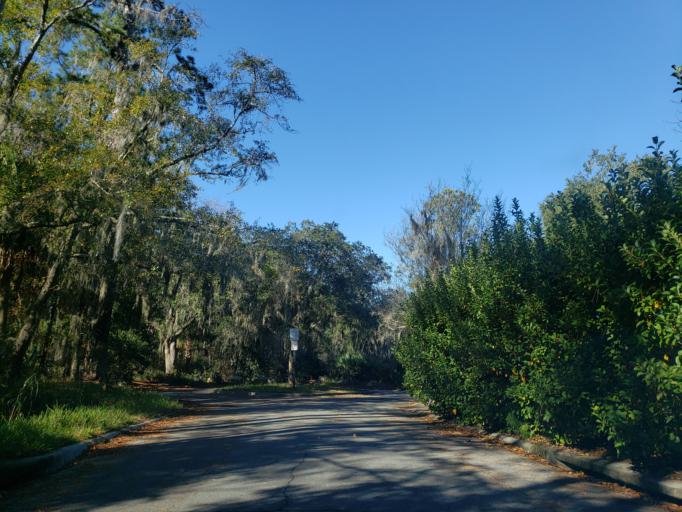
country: US
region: Georgia
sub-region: Chatham County
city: Isle of Hope
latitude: 31.9808
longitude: -81.0686
